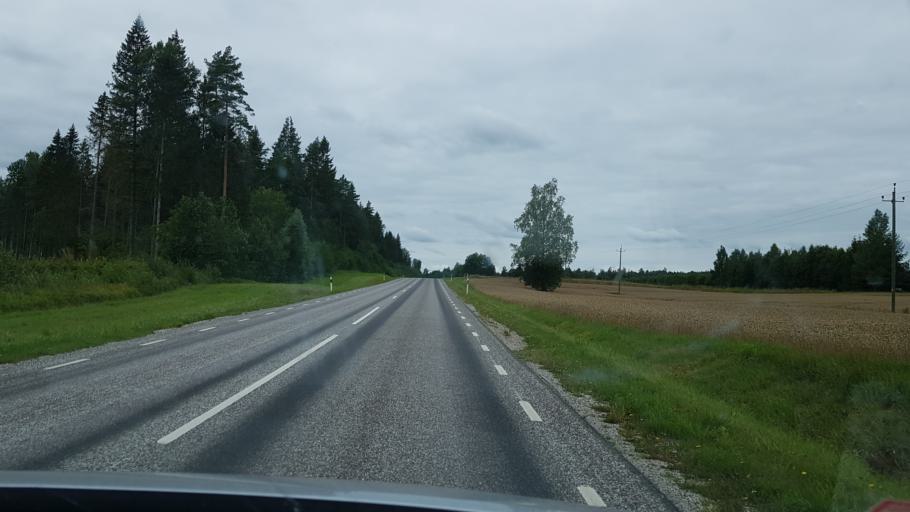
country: EE
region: Vorumaa
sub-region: Antsla vald
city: Vana-Antsla
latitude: 57.9999
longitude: 26.7159
